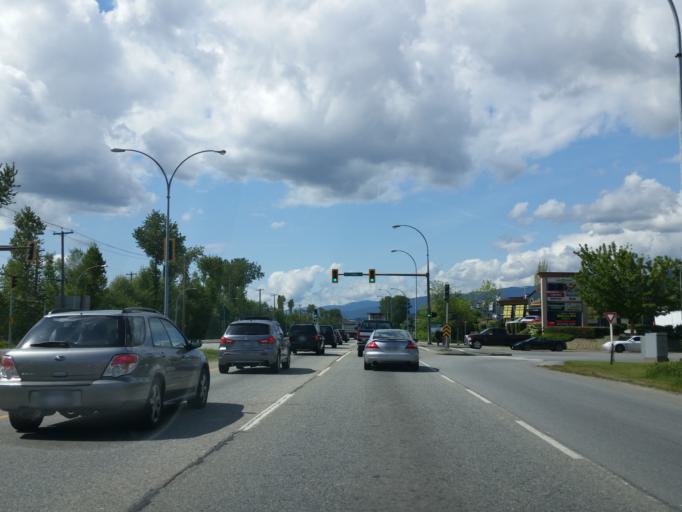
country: CA
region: British Columbia
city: Coquitlam
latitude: 49.2553
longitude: -122.7469
